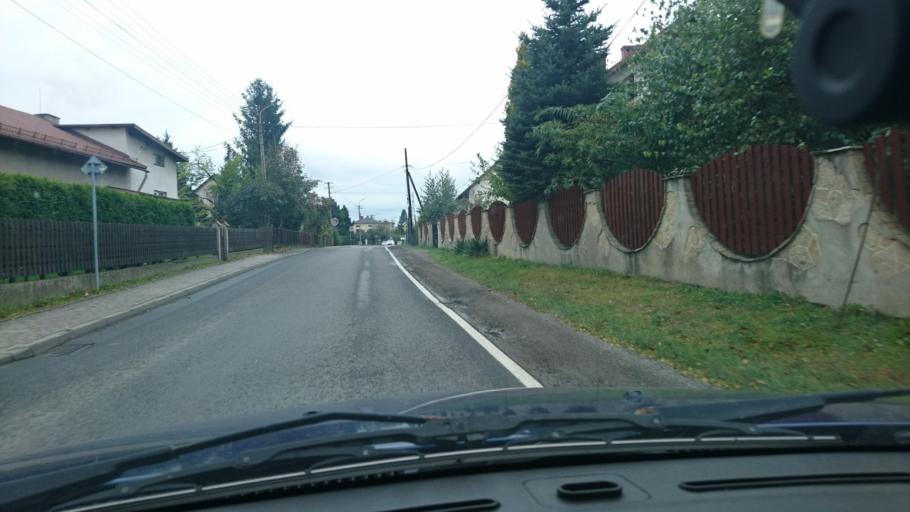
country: PL
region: Silesian Voivodeship
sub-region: Powiat bielski
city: Kozy
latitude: 49.8533
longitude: 19.1403
